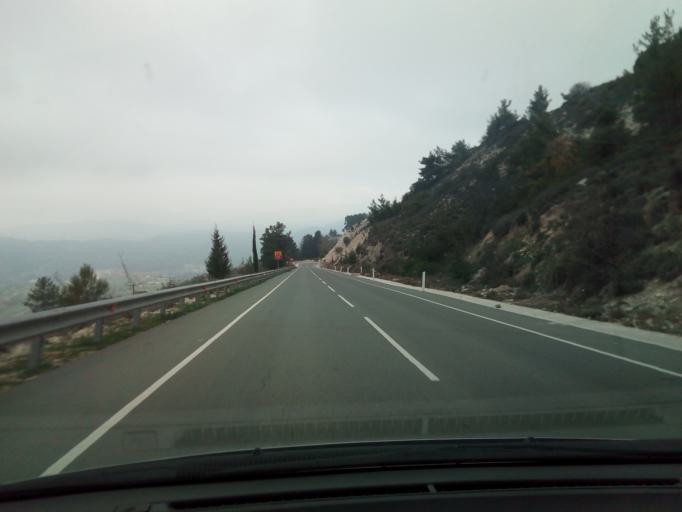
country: CY
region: Pafos
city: Mesogi
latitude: 34.9030
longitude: 32.6177
